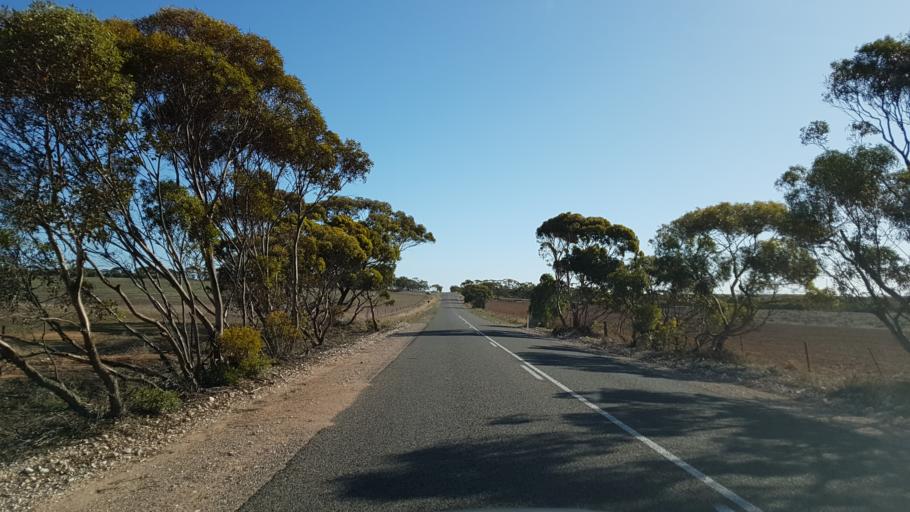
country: AU
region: South Australia
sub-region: Mid Murray
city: Mannum
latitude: -34.7798
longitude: 139.5317
